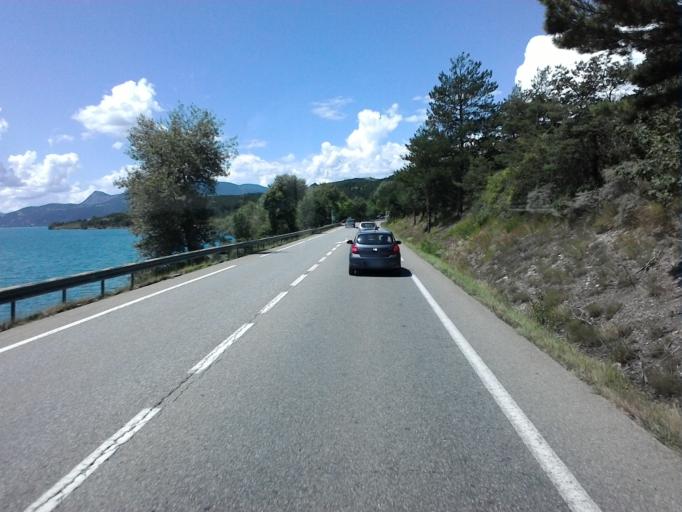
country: FR
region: Provence-Alpes-Cote d'Azur
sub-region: Departement des Hautes-Alpes
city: Chorges
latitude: 44.5356
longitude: 6.3875
